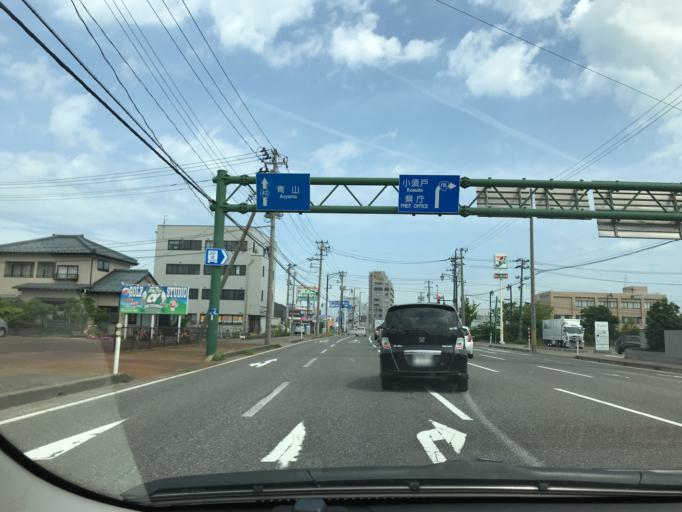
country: JP
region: Niigata
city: Niigata-shi
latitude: 37.8805
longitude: 139.0130
